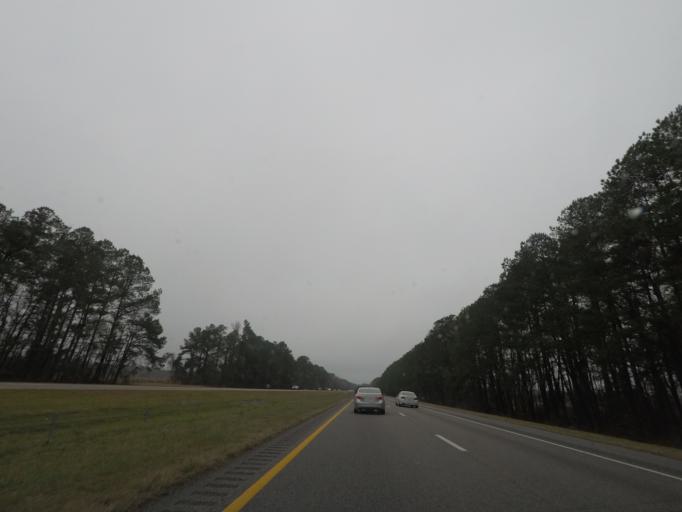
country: US
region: South Carolina
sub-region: Florence County
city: Timmonsville
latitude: 33.9412
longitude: -80.0620
